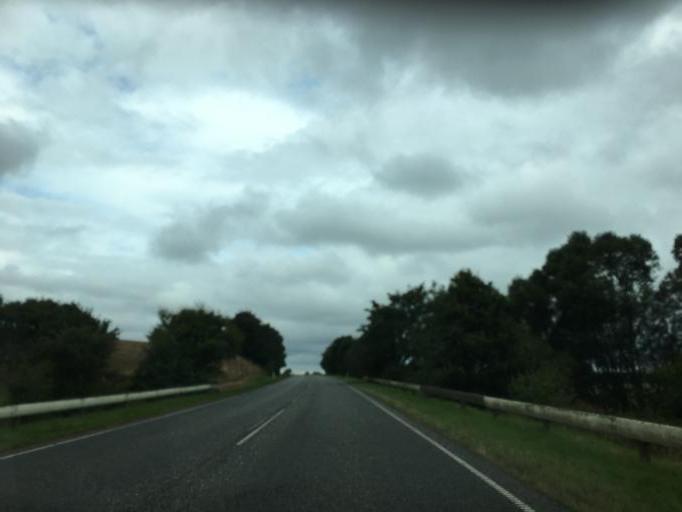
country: DK
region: South Denmark
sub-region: Kolding Kommune
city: Kolding
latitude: 55.5823
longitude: 9.4987
